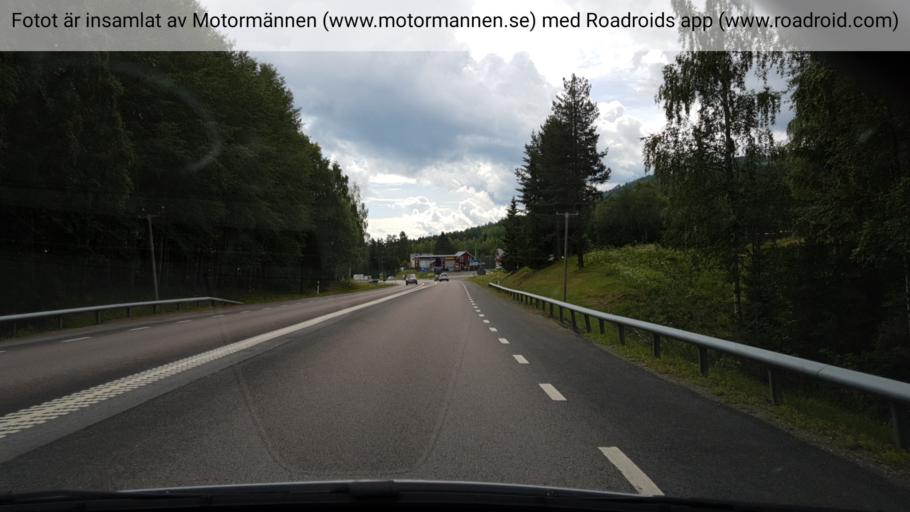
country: SE
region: Vaesternorrland
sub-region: Solleftea Kommun
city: Solleftea
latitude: 63.1724
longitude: 17.2275
